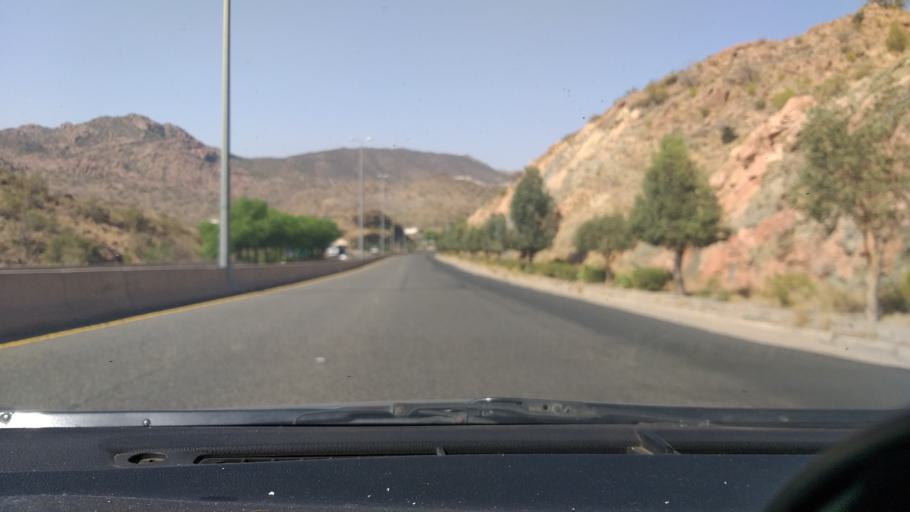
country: SA
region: Makkah
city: Ash Shafa
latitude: 21.1097
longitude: 40.3443
